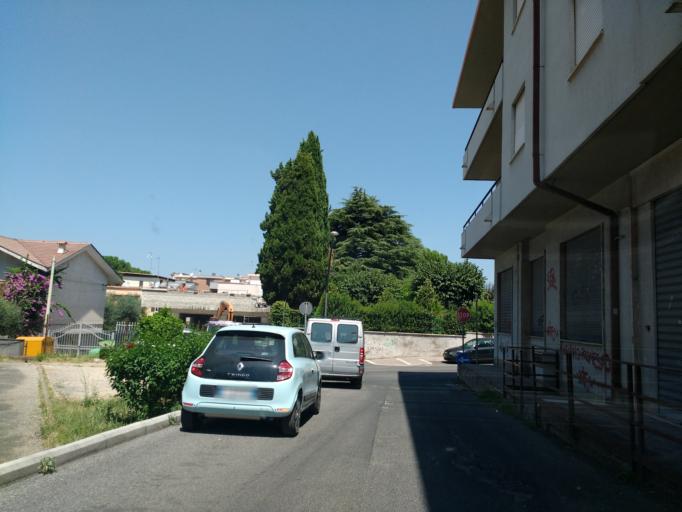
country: IT
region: Latium
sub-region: Citta metropolitana di Roma Capitale
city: Villa Adriana
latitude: 41.9521
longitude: 12.7755
